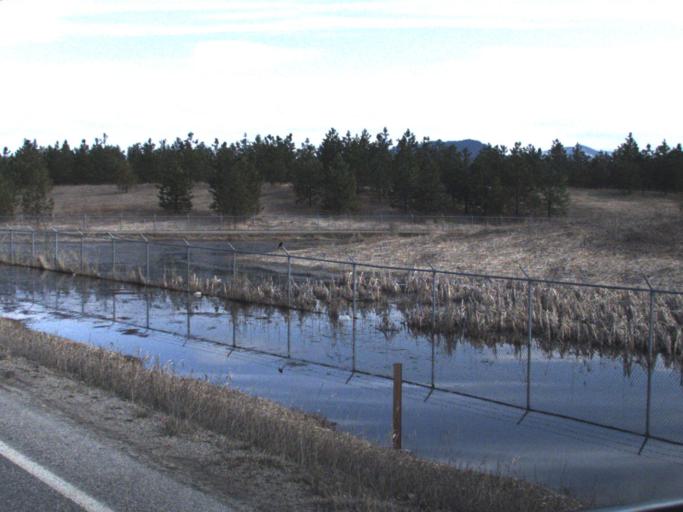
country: US
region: Washington
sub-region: Pend Oreille County
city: Newport
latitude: 48.2952
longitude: -117.2772
